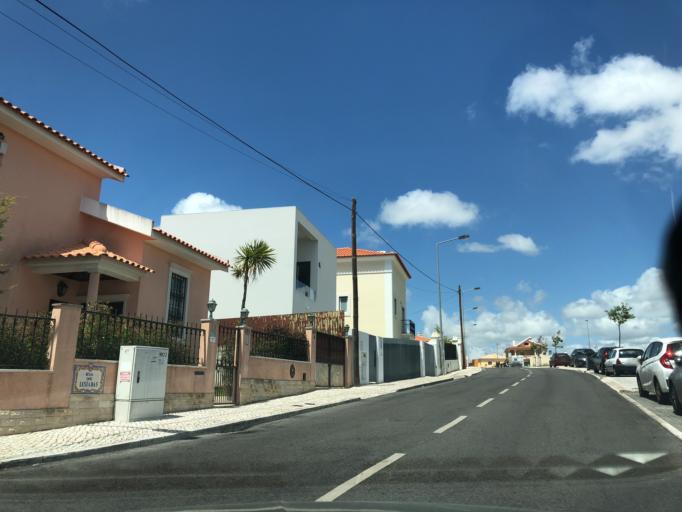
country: PT
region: Lisbon
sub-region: Cascais
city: Sao Domingos de Rana
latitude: 38.7045
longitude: -9.3290
